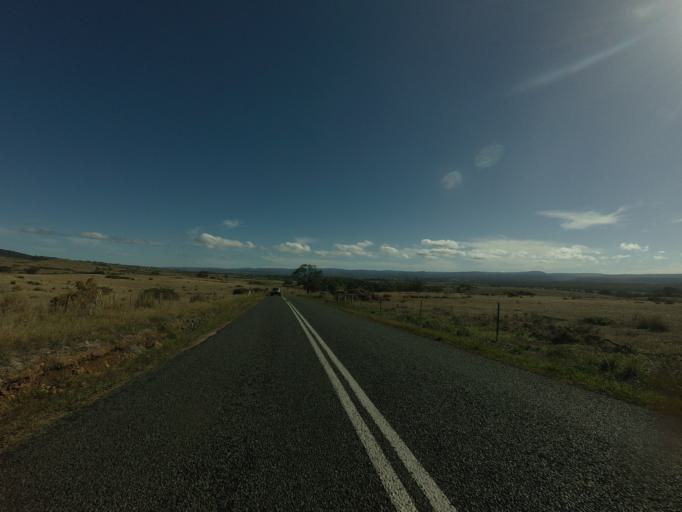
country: AU
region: Tasmania
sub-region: Break O'Day
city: St Helens
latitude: -41.9964
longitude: 148.0932
